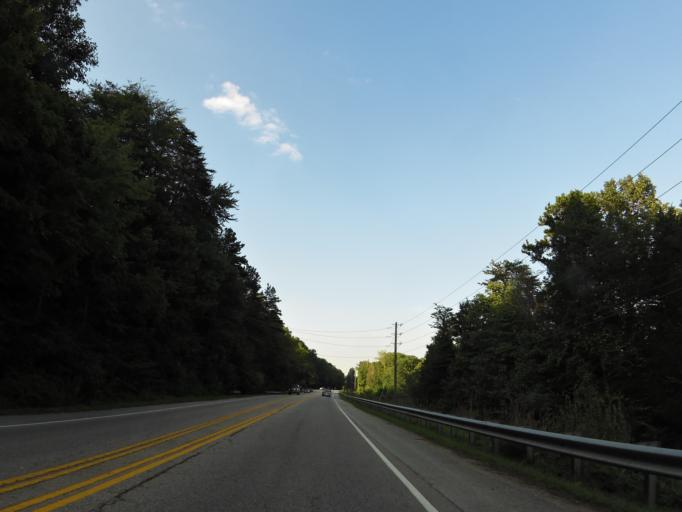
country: US
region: Tennessee
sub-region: Anderson County
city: Oak Ridge
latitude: 36.0128
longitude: -84.1729
